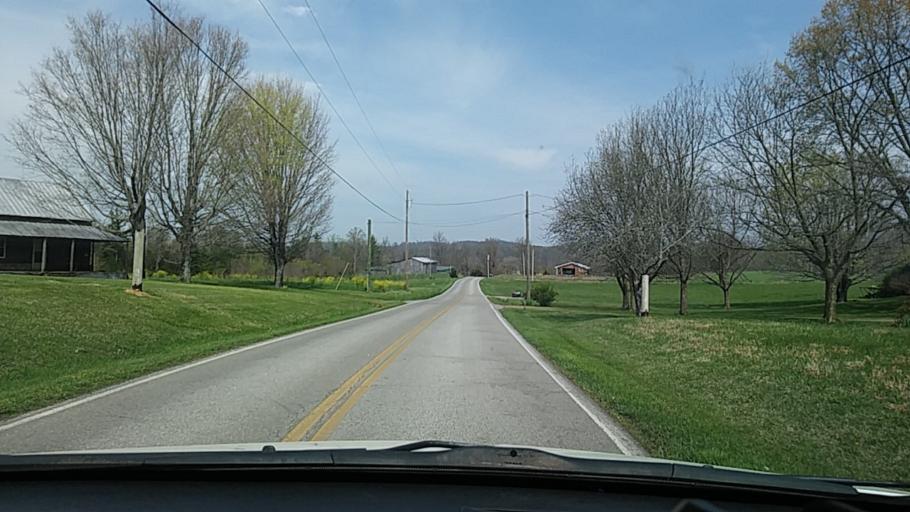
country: US
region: Tennessee
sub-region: Greene County
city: Tusculum
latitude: 36.0935
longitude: -82.7159
